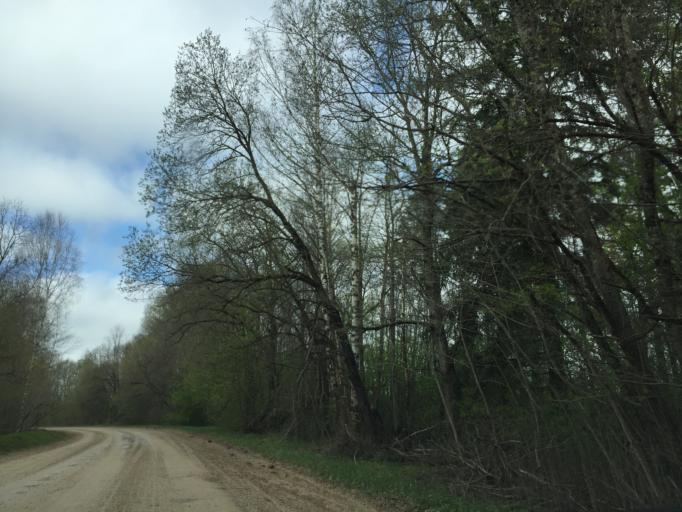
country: LV
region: Apes Novads
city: Ape
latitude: 57.5364
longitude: 26.3490
